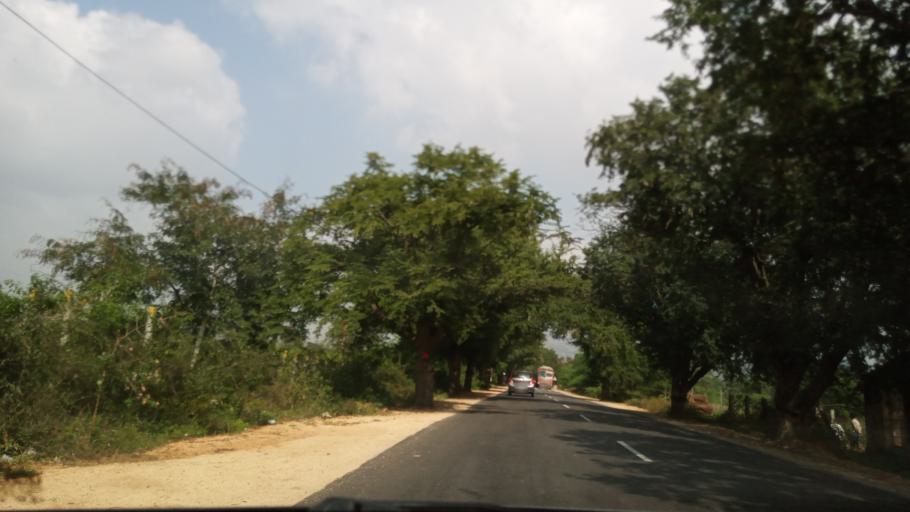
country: IN
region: Andhra Pradesh
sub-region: Chittoor
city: Madanapalle
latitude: 13.6240
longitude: 78.5483
